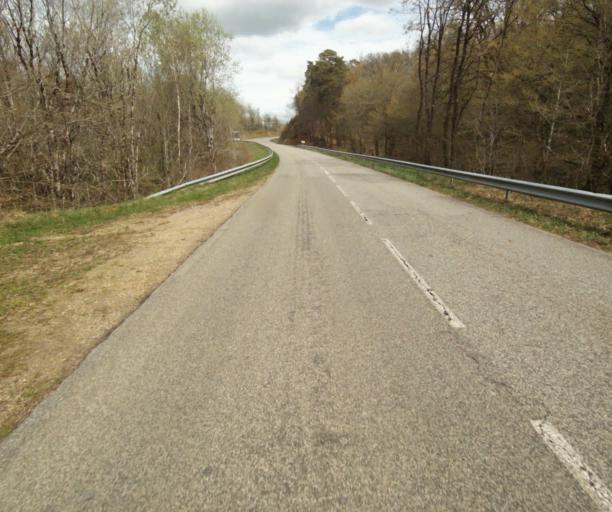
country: FR
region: Limousin
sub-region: Departement de la Correze
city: Laguenne
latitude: 45.2084
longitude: 1.8636
